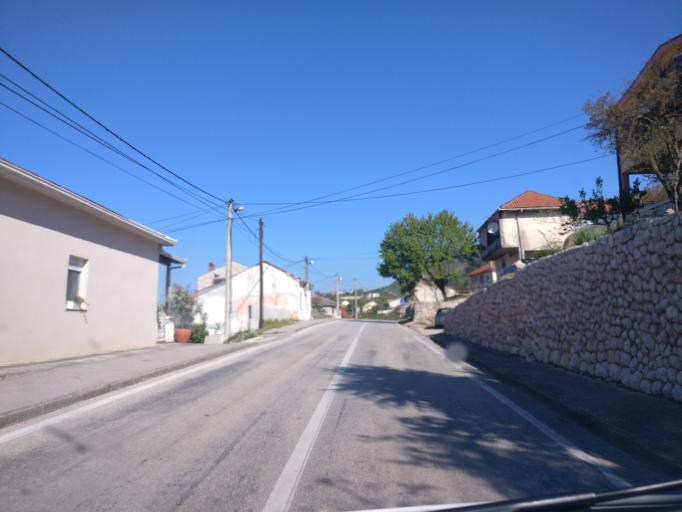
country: BA
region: Federation of Bosnia and Herzegovina
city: Capljina
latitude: 43.1367
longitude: 17.6716
